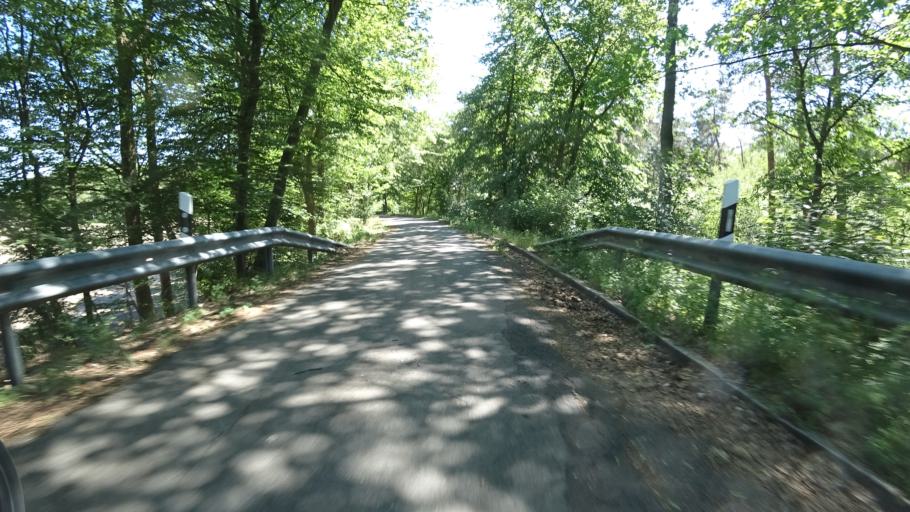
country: DE
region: North Rhine-Westphalia
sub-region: Regierungsbezirk Detmold
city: Guetersloh
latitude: 51.8616
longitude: 8.3566
